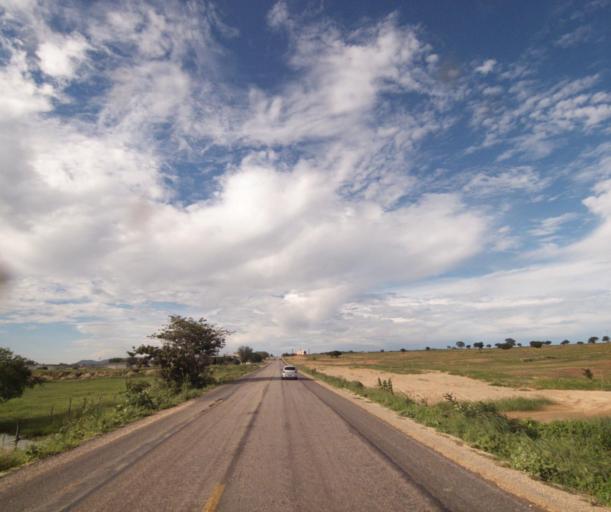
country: BR
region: Bahia
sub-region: Guanambi
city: Guanambi
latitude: -14.2725
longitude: -42.7831
